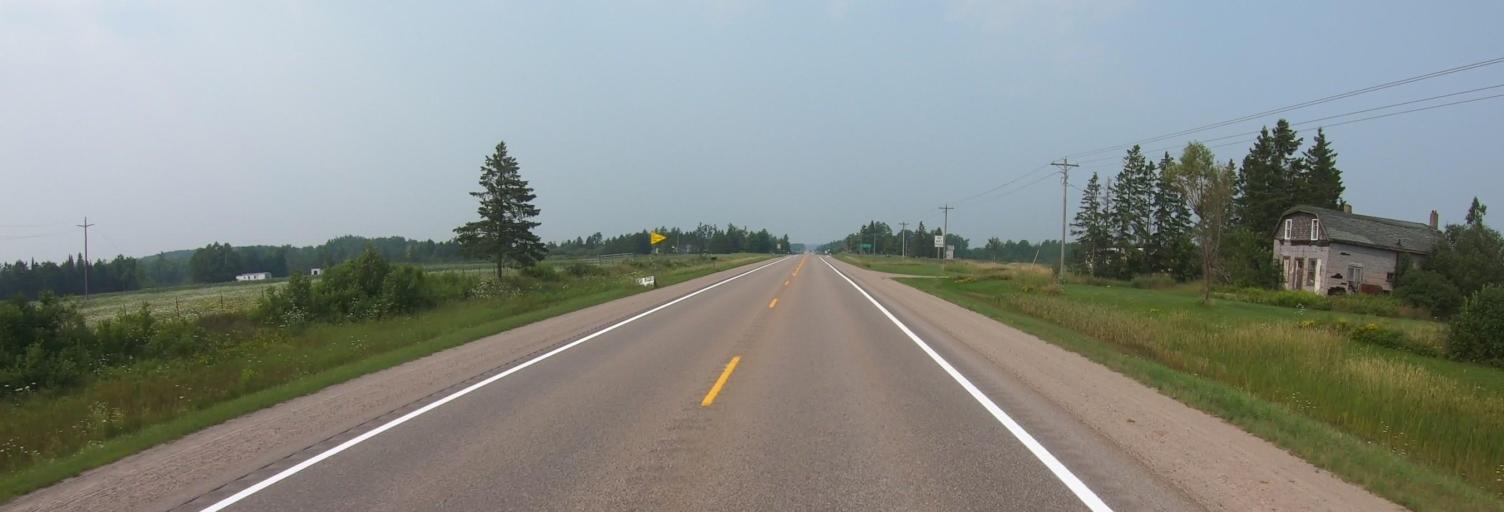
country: US
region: Michigan
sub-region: Chippewa County
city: Sault Ste. Marie
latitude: 46.3284
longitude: -84.3639
